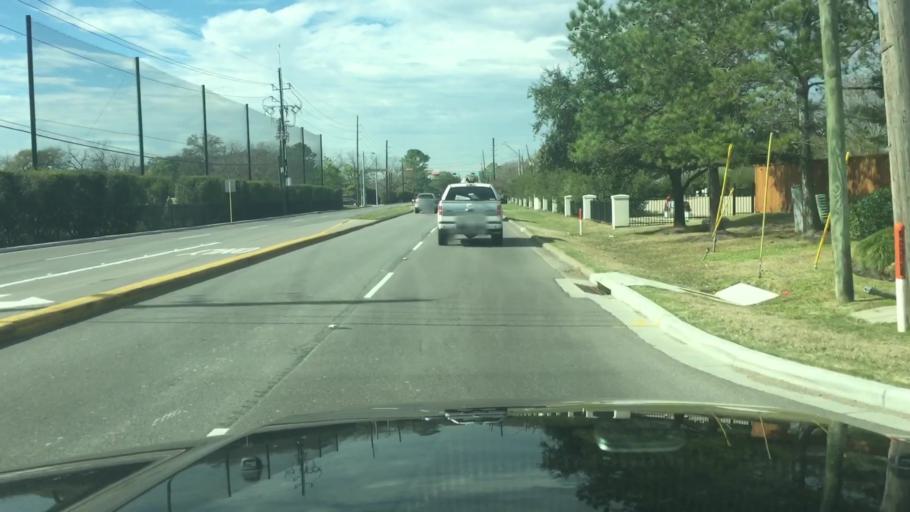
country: US
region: Texas
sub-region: Harris County
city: Oak Cliff Place
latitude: 29.8312
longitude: -95.6734
